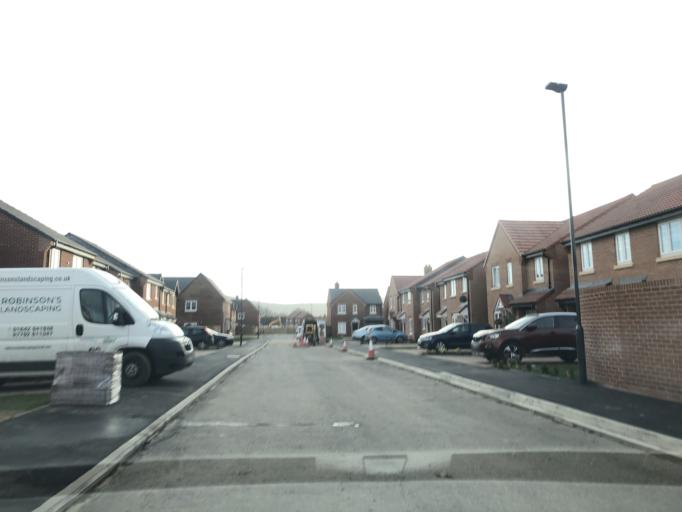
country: GB
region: England
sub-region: North Yorkshire
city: Stokesley
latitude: 54.4708
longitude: -1.2034
